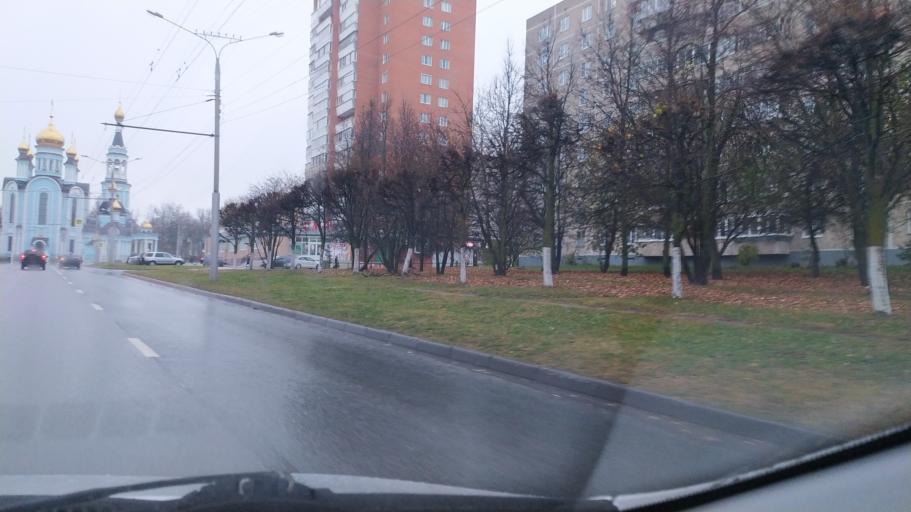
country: RU
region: Chuvashia
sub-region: Cheboksarskiy Rayon
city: Cheboksary
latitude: 56.1424
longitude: 47.1859
